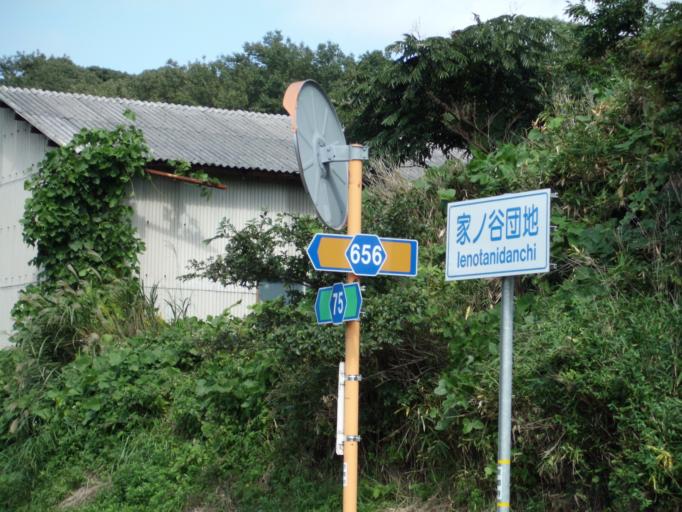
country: JP
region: Kyoto
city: Miyazu
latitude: 35.7290
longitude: 135.1035
